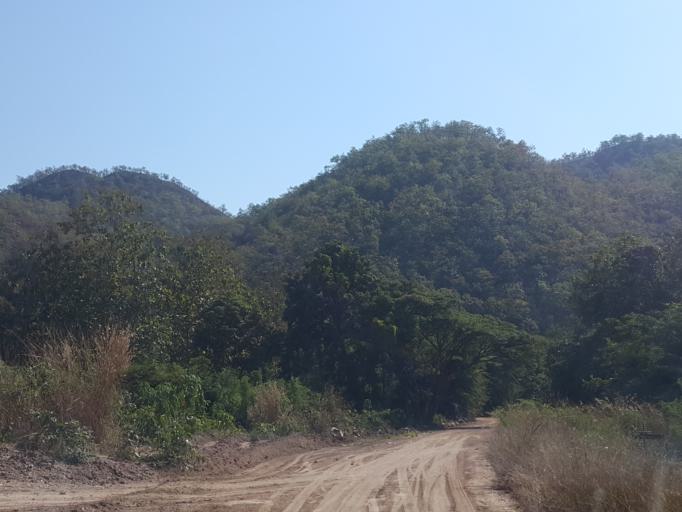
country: TH
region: Sukhothai
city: Thung Saliam
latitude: 17.3215
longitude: 99.4626
